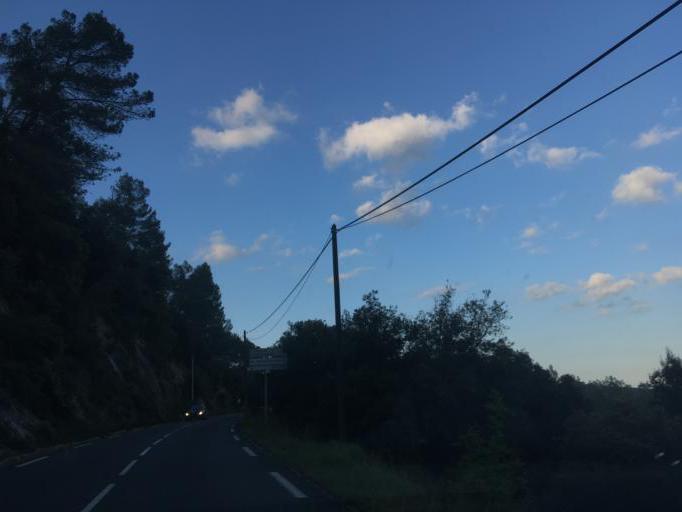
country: FR
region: Provence-Alpes-Cote d'Azur
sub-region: Departement du Var
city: Carces
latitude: 43.4845
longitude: 6.2130
